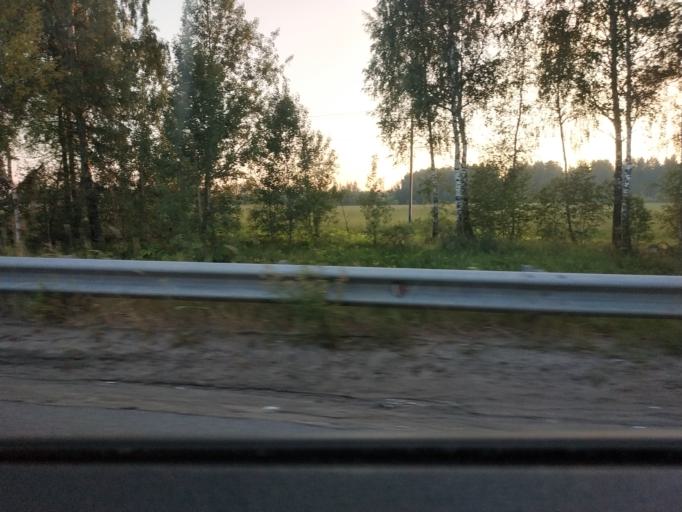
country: RU
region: Moskovskaya
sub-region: Shchelkovskiy Rayon
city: Grebnevo
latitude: 56.0000
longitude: 38.1291
